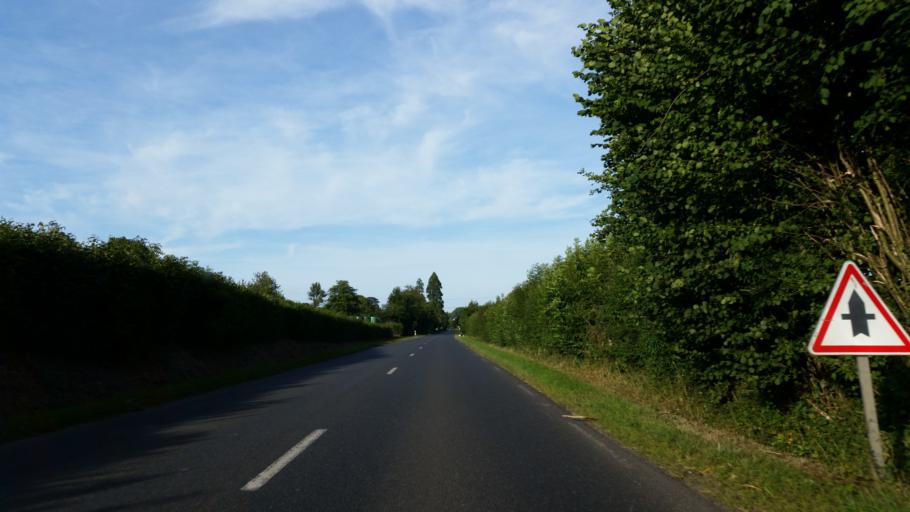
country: FR
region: Lower Normandy
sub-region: Departement du Calvados
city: Cambremer
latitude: 49.1940
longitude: 0.0582
